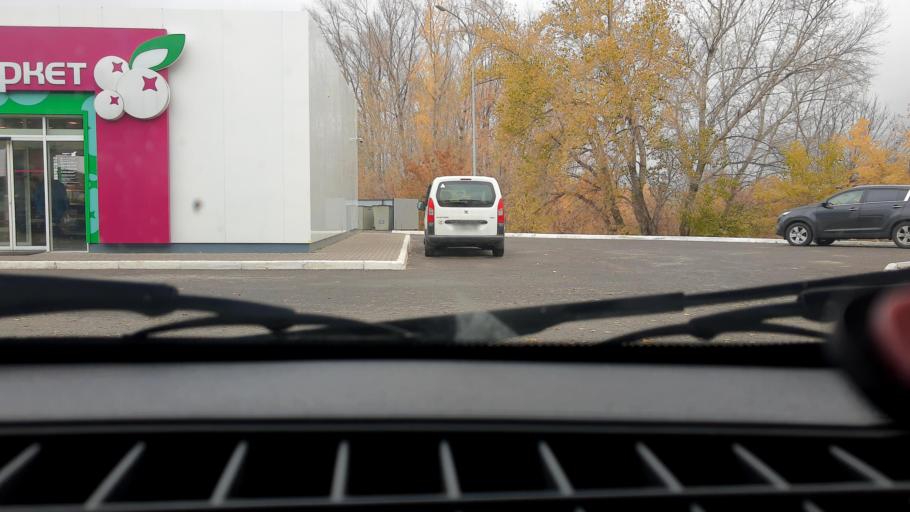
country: RU
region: Bashkortostan
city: Ufa
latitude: 54.6128
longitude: 55.9238
